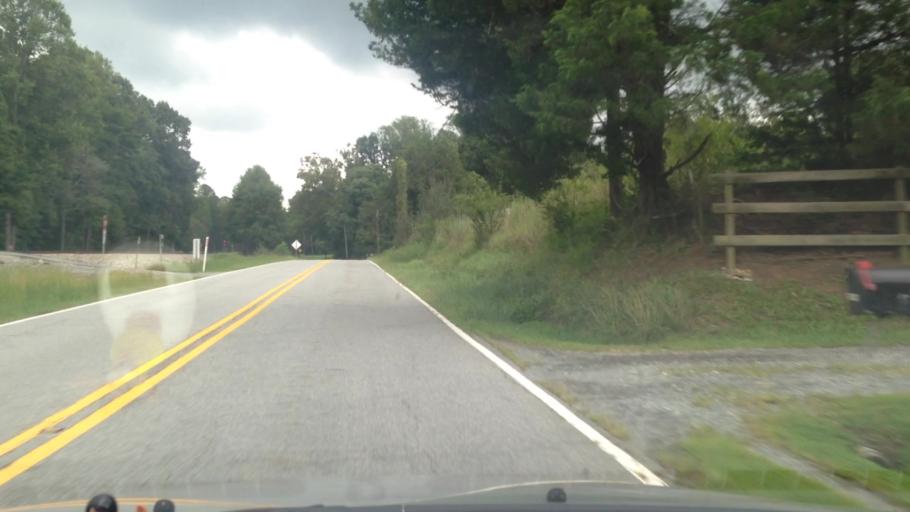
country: US
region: North Carolina
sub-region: Forsyth County
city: Walkertown
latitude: 36.2068
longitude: -80.1694
